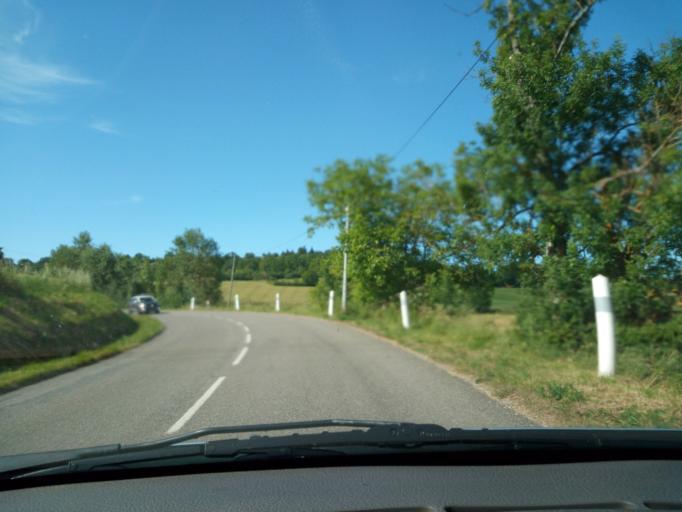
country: FR
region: Midi-Pyrenees
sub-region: Departement du Lot
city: Castelnau-Montratier
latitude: 44.2625
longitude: 1.3618
